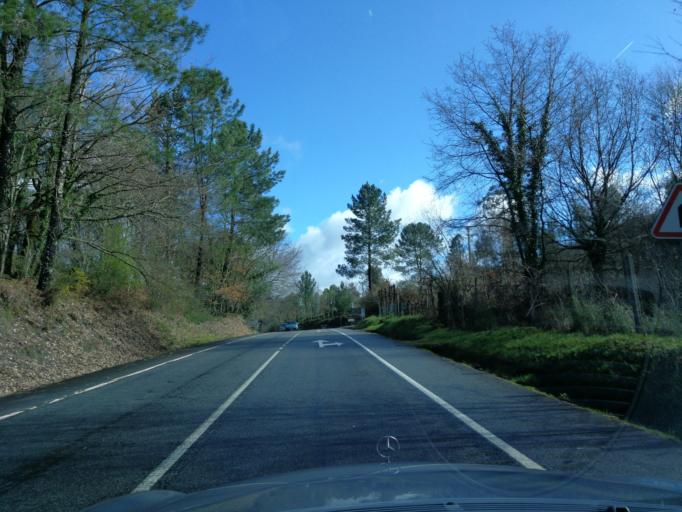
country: PT
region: Viana do Castelo
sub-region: Ponte da Barca
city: Ponte da Barca
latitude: 41.8102
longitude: -8.3421
